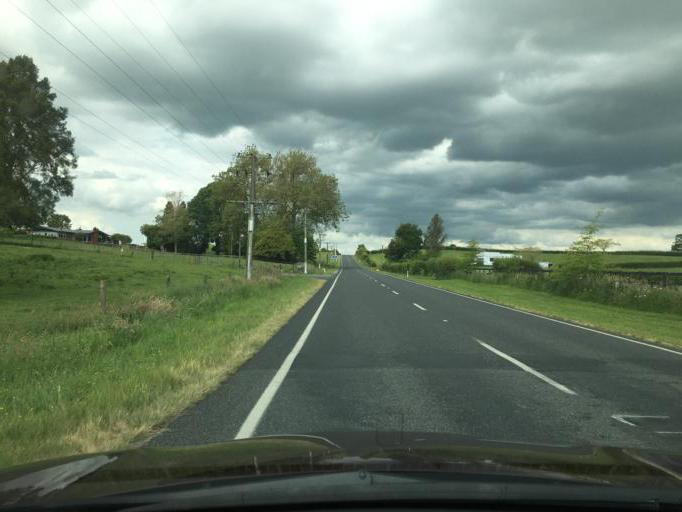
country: NZ
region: Waikato
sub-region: Waipa District
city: Cambridge
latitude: -38.0030
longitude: 175.3834
